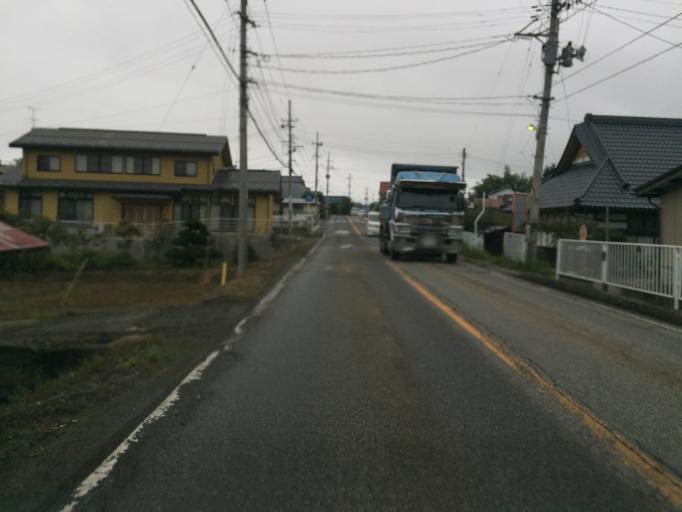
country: JP
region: Fukushima
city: Kitakata
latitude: 37.4347
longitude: 139.9180
